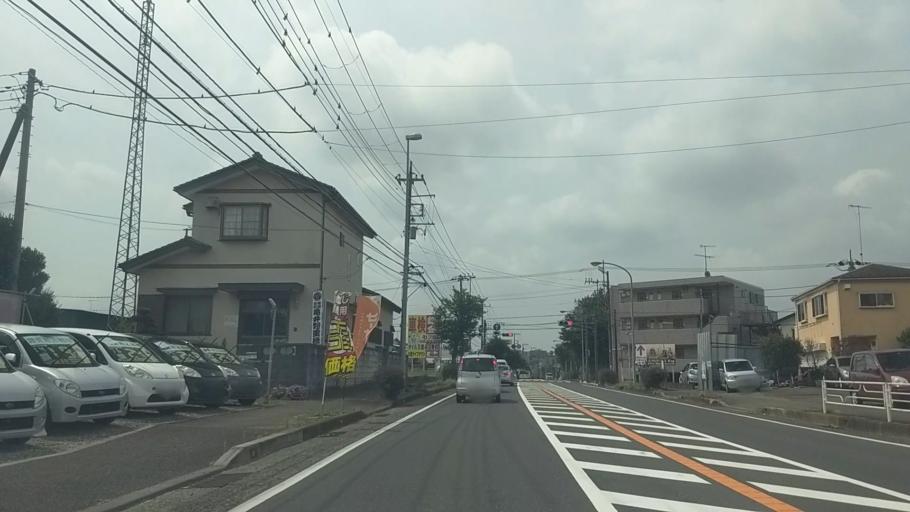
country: JP
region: Kanagawa
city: Fujisawa
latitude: 35.3717
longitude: 139.4788
